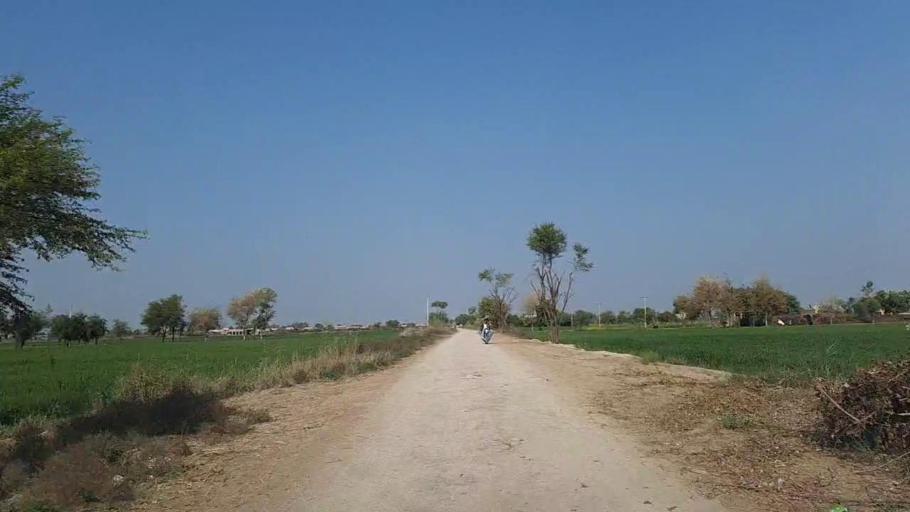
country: PK
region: Sindh
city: Nawabshah
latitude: 26.2836
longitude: 68.5136
